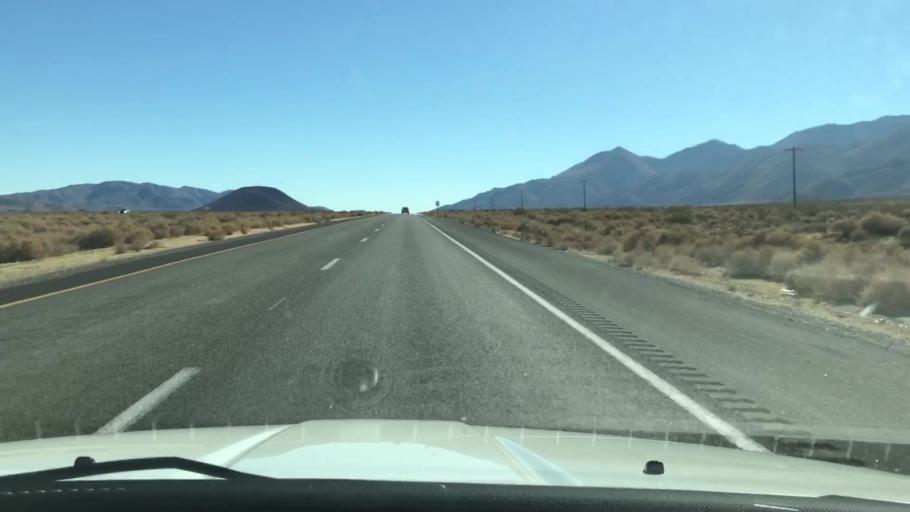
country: US
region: California
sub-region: Kern County
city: Inyokern
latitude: 36.0352
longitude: -117.9446
